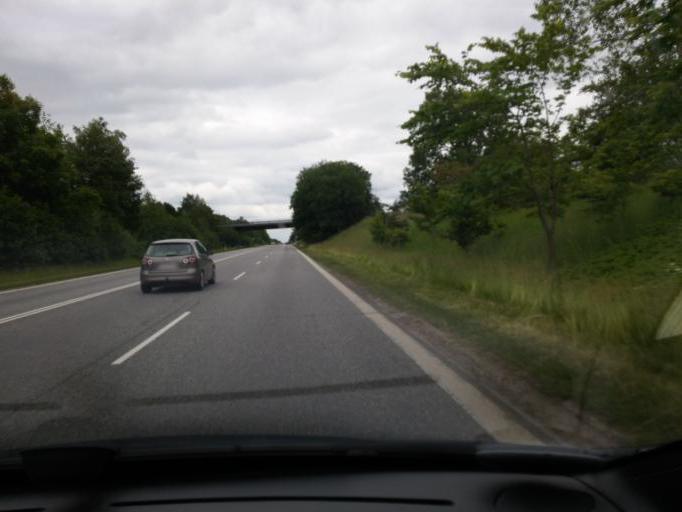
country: DK
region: Capital Region
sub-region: Hillerod Kommune
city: Hillerod
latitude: 55.9297
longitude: 12.2522
